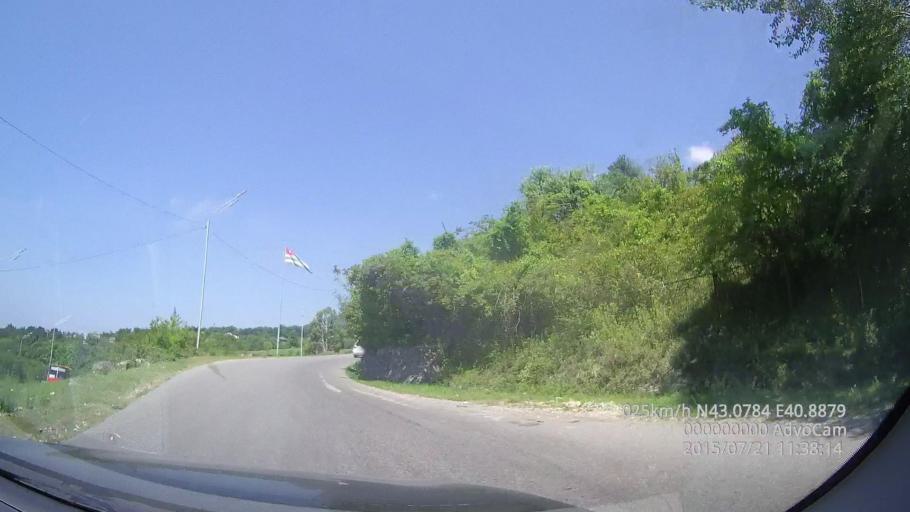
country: GE
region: Abkhazia
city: Stantsiya Novyy Afon
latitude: 43.0786
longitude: 40.8879
